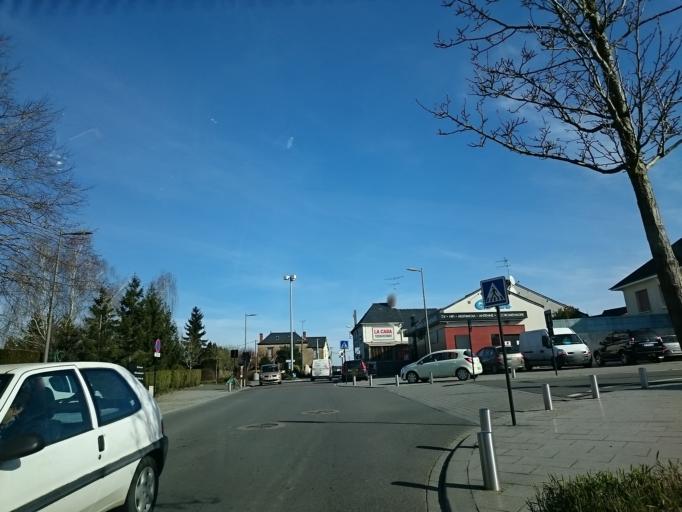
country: FR
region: Brittany
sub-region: Departement d'Ille-et-Vilaine
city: Vern-sur-Seiche
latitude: 48.0475
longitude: -1.6024
